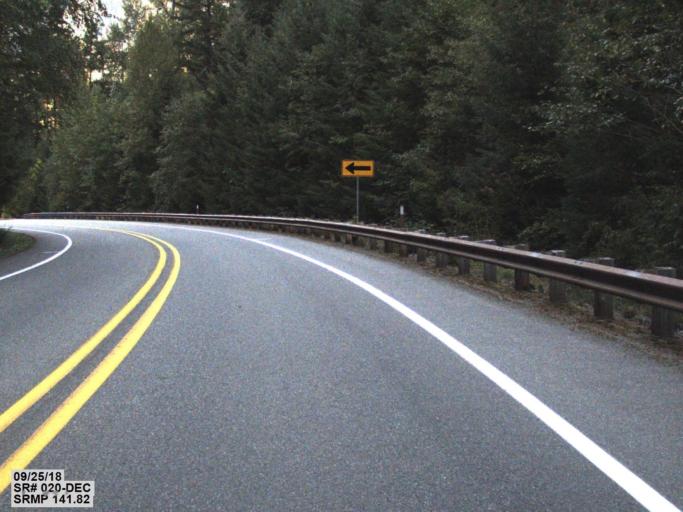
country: US
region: Washington
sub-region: Snohomish County
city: Darrington
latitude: 48.7017
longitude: -120.9072
